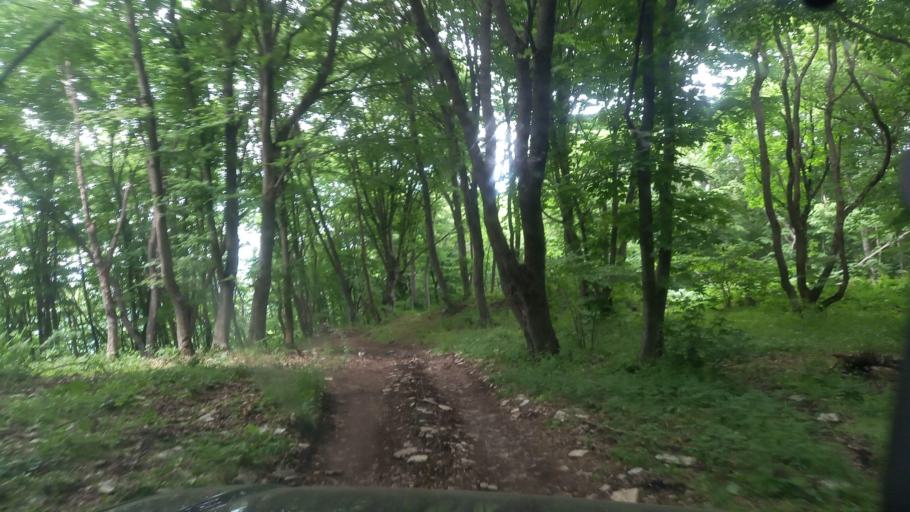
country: RU
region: Karachayevo-Cherkesiya
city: Pregradnaya
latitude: 44.0116
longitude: 41.2805
